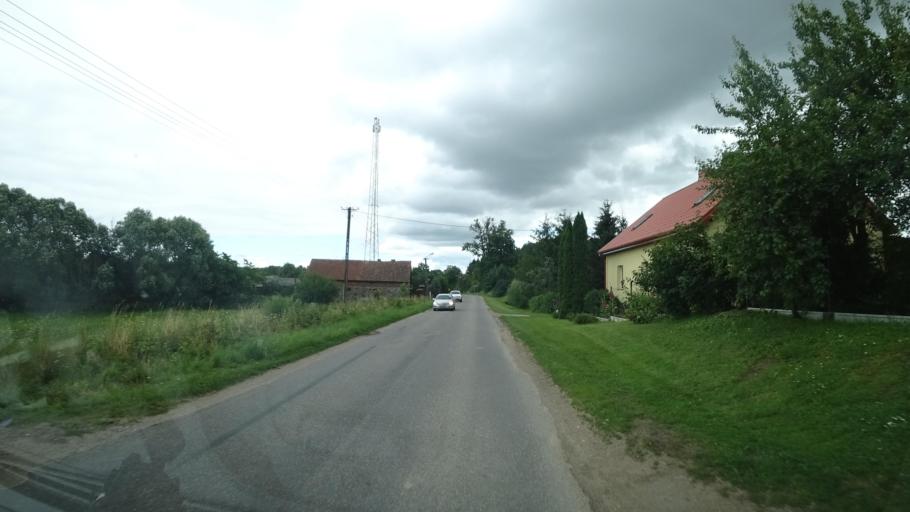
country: PL
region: Podlasie
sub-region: Powiat suwalski
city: Filipow
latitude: 54.2846
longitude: 22.5199
